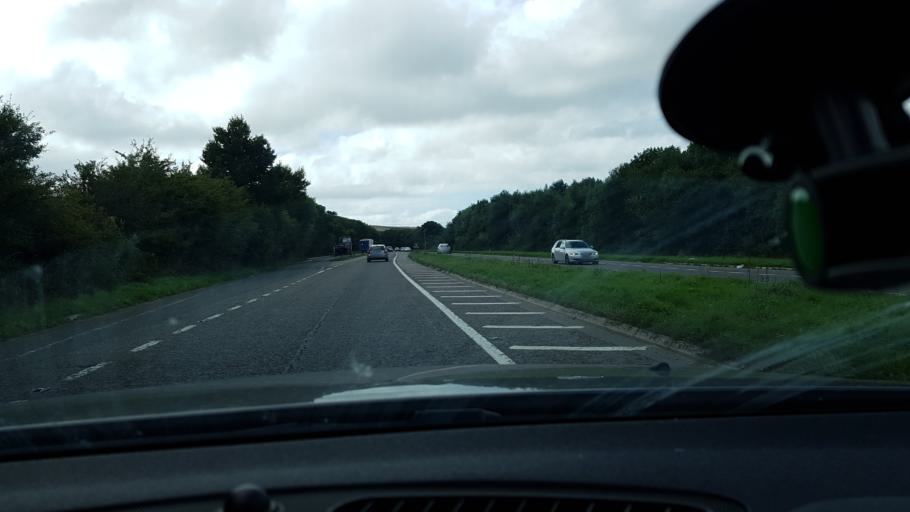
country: GB
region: England
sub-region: Cornwall
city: Perranporth
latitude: 50.2964
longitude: -5.1268
